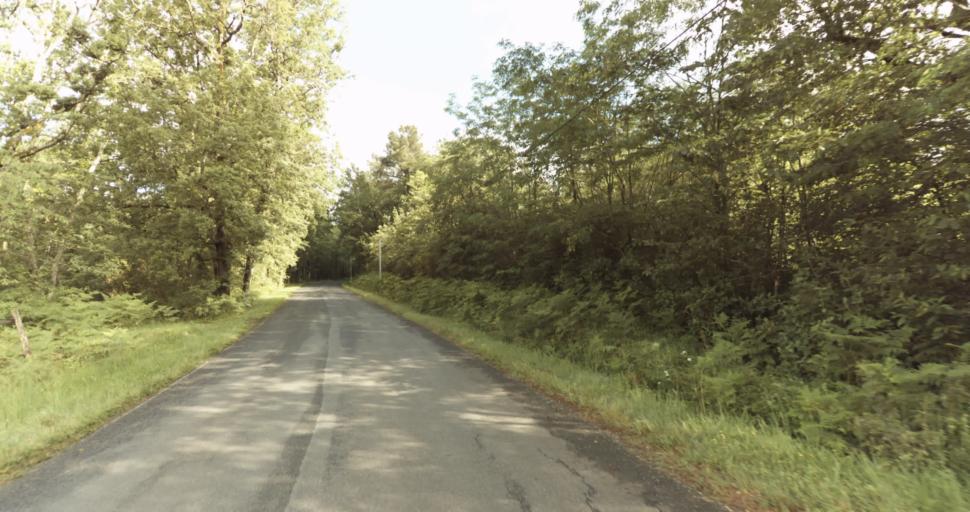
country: FR
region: Aquitaine
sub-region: Departement de la Dordogne
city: Le Bugue
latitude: 44.9271
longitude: 0.8212
